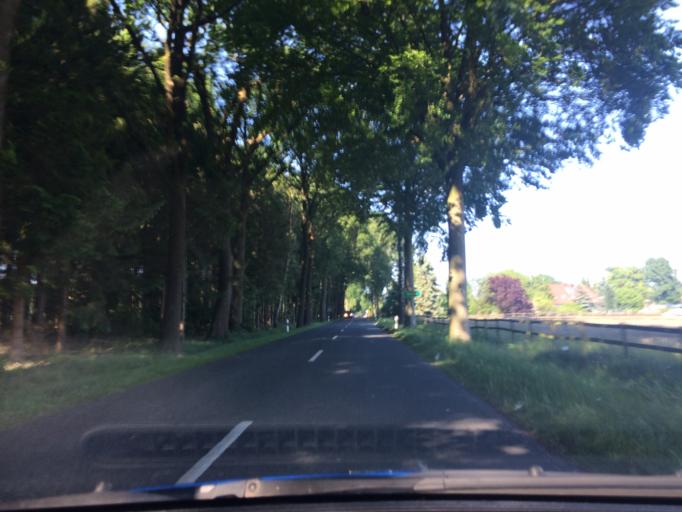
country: DE
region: Lower Saxony
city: Bomlitz
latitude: 52.9573
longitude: 9.6992
